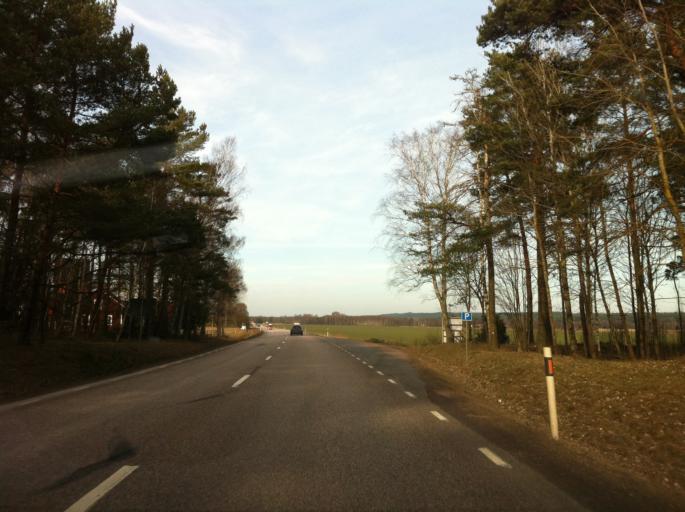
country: SE
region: Vaestra Goetaland
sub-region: Gullspangs Kommun
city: Gullspang
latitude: 59.1045
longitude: 14.1710
